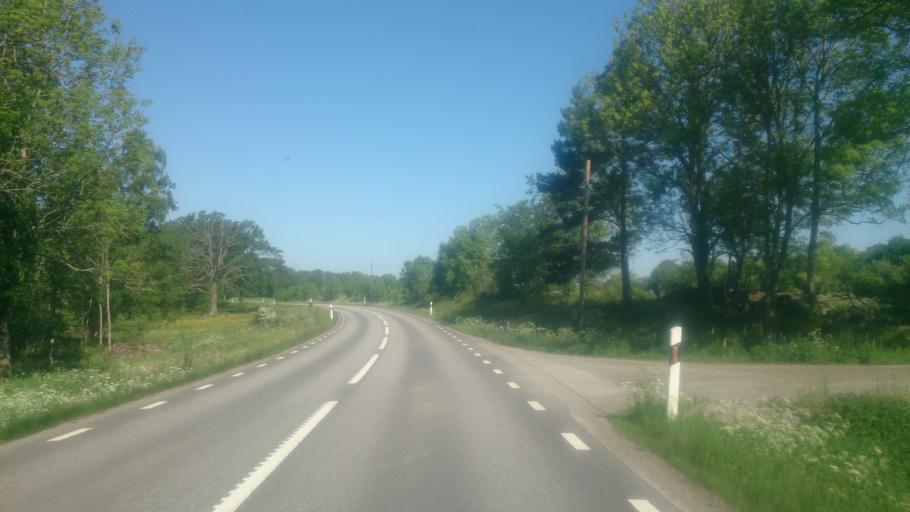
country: SE
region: OEstergoetland
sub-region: Atvidabergs Kommun
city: Atvidaberg
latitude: 58.1383
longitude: 16.0888
